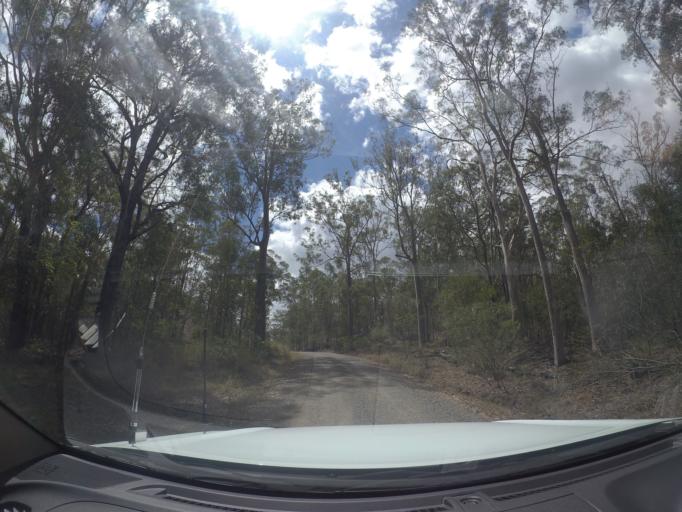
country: AU
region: Queensland
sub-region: Logan
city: Cedar Vale
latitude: -27.9041
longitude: 153.0319
